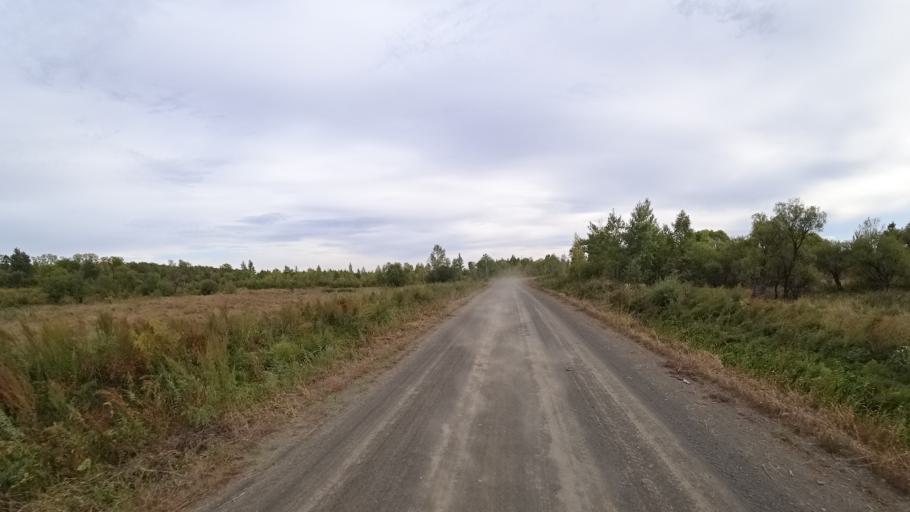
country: RU
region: Amur
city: Arkhara
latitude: 49.3170
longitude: 130.1829
